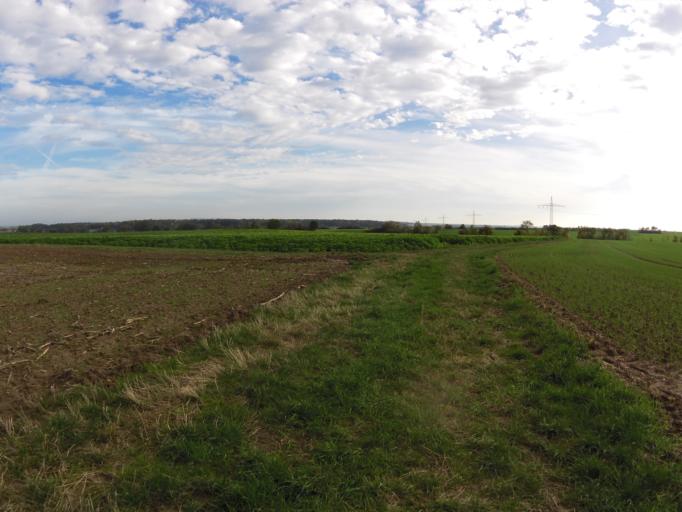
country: DE
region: Bavaria
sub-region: Regierungsbezirk Unterfranken
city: Biebelried
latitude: 49.7307
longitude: 10.0705
